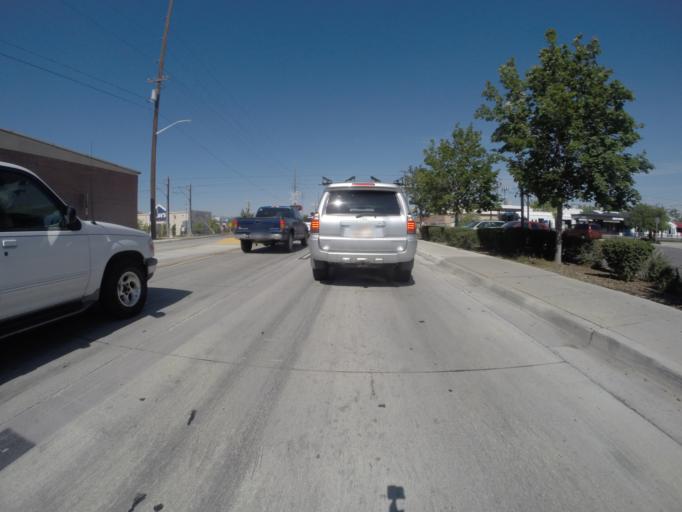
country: US
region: Utah
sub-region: Salt Lake County
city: Salt Lake City
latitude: 40.7416
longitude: -111.8963
